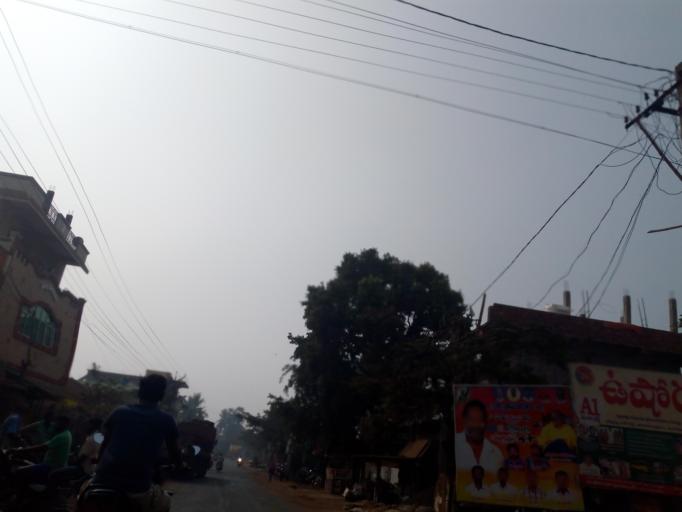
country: IN
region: Andhra Pradesh
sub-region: West Godavari
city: Tadepallegudem
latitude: 16.8189
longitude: 81.4054
